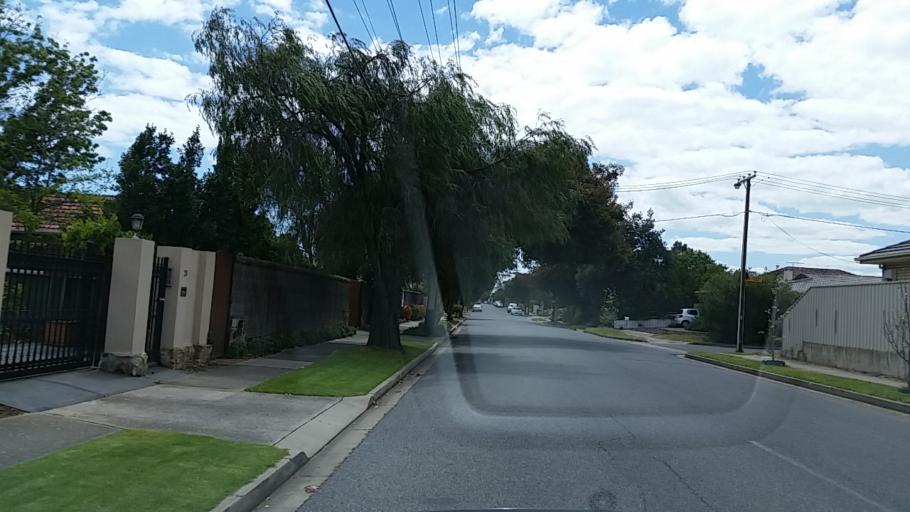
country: AU
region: South Australia
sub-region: Holdfast Bay
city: North Brighton
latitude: -34.9943
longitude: 138.5162
